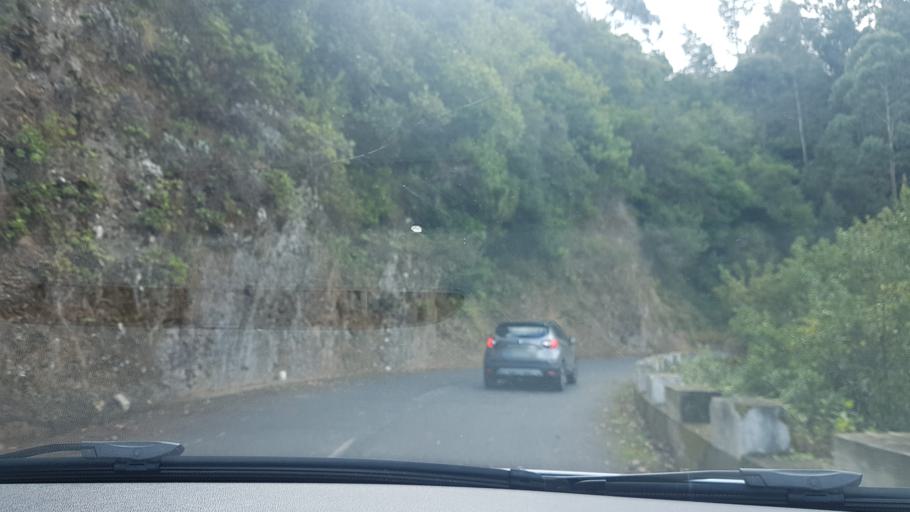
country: PT
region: Madeira
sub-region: Sao Vicente
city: Sao Vicente
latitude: 32.7716
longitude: -17.0265
